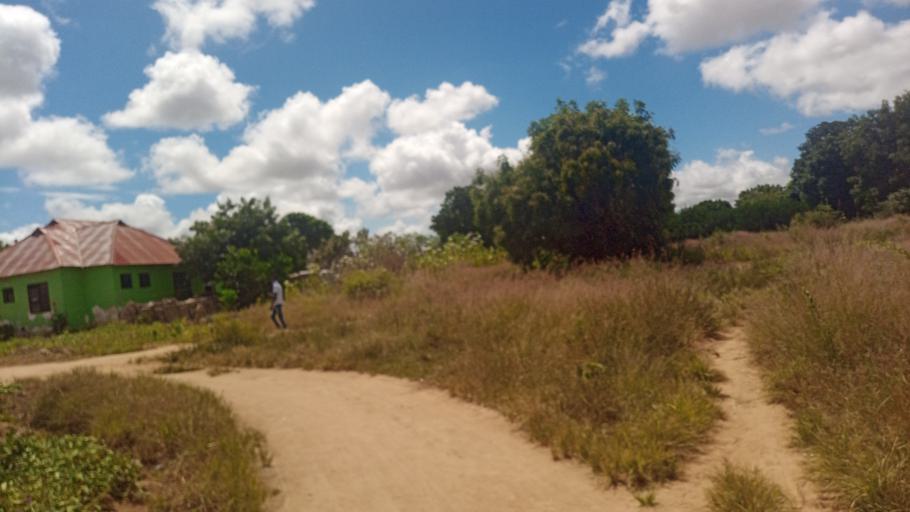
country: TZ
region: Dodoma
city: Kisasa
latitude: -6.1776
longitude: 35.7688
